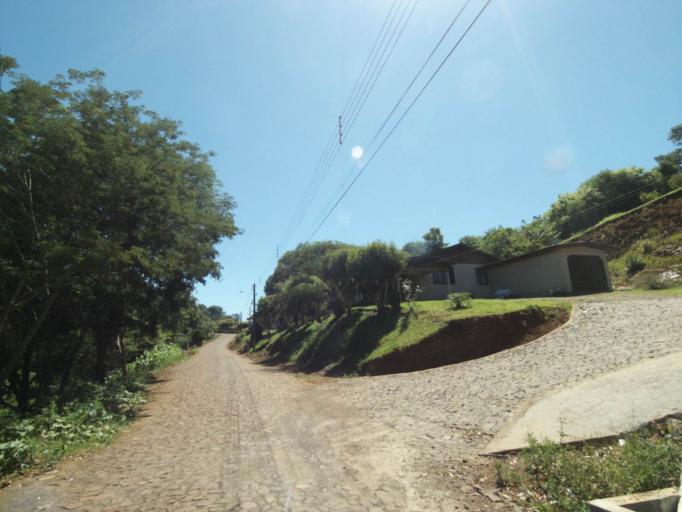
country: BR
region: Parana
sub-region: Ampere
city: Ampere
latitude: -26.1779
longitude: -53.3587
